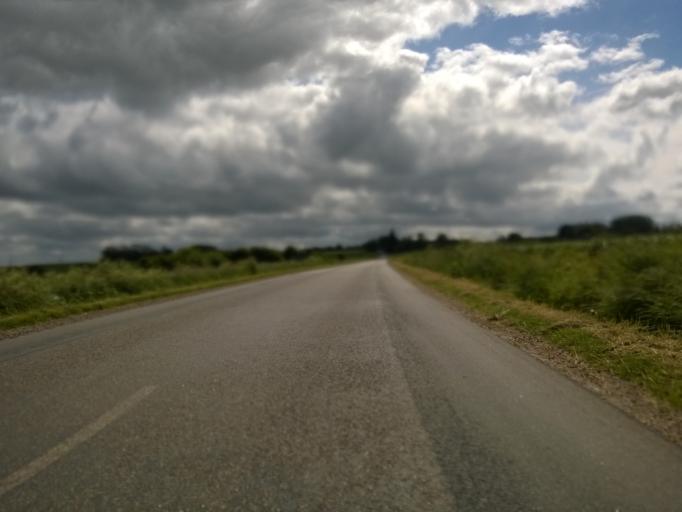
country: DK
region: Central Jutland
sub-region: Holstebro Kommune
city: Vinderup
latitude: 56.4436
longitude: 8.8636
